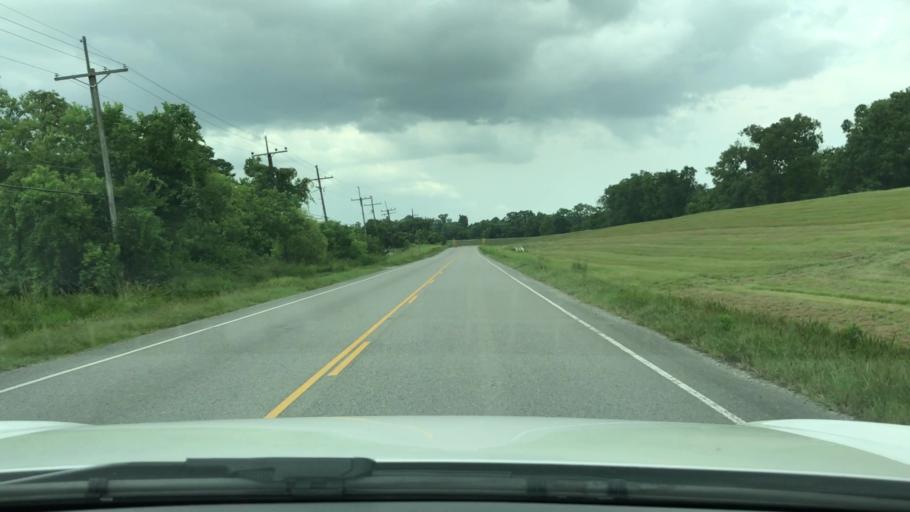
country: US
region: Louisiana
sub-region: Iberville Parish
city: Saint Gabriel
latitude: 30.2725
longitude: -91.1565
